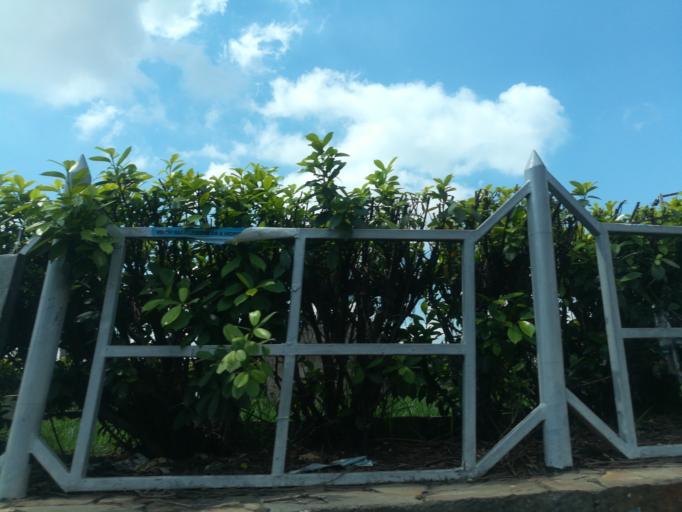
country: NG
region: Oyo
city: Ibadan
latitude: 7.3603
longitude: 3.8703
